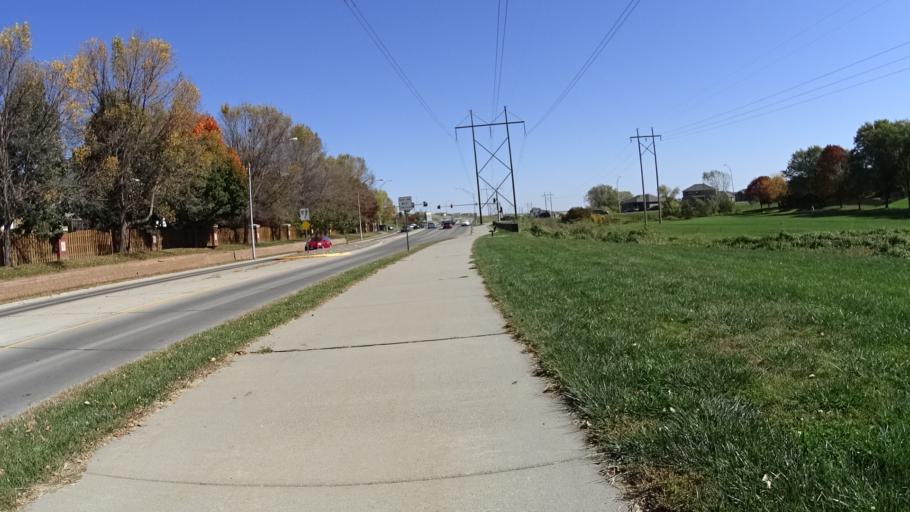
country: US
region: Nebraska
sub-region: Sarpy County
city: La Vista
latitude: 41.1693
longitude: -96.0255
